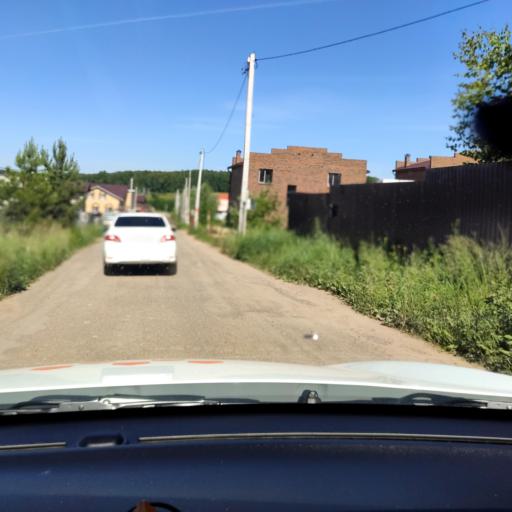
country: RU
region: Tatarstan
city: Vysokaya Gora
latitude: 55.8175
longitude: 49.2853
